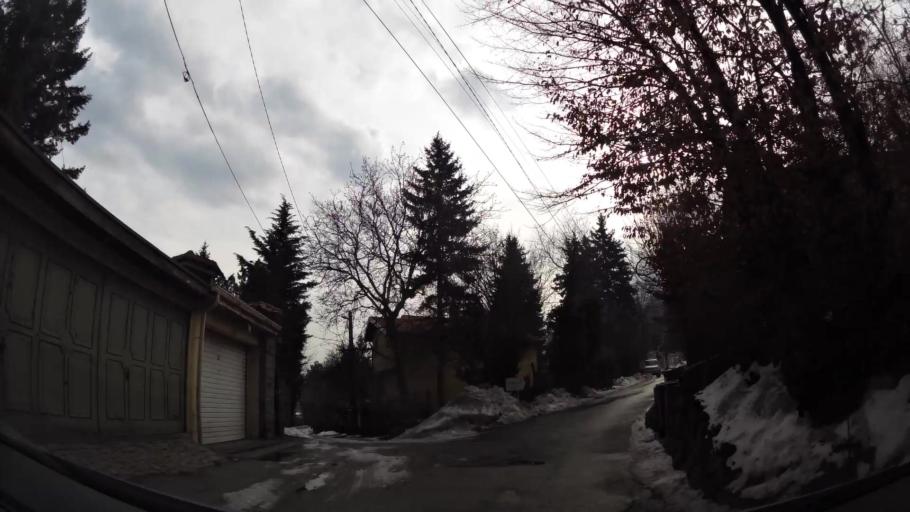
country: BG
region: Sofia-Capital
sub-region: Stolichna Obshtina
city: Sofia
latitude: 42.6437
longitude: 23.2785
